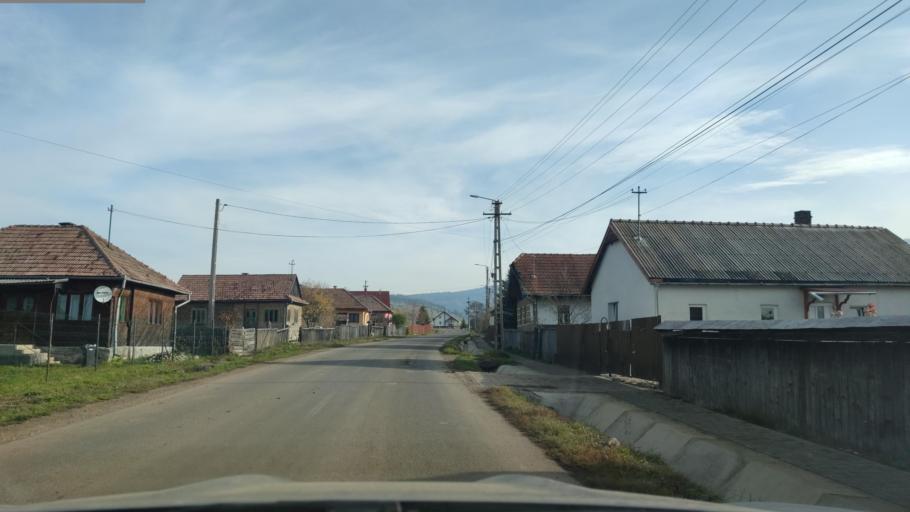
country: RO
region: Harghita
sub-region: Comuna Ditrau
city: Ditrau
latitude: 46.8187
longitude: 25.5250
